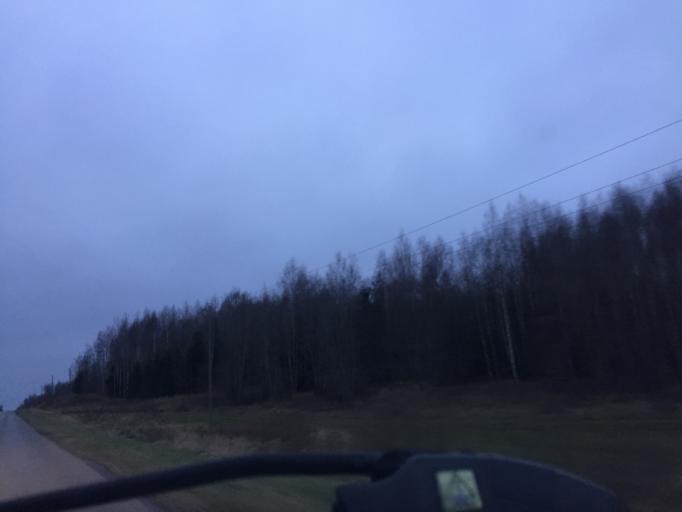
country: LV
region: Limbazu Rajons
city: Limbazi
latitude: 57.6057
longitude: 24.8106
